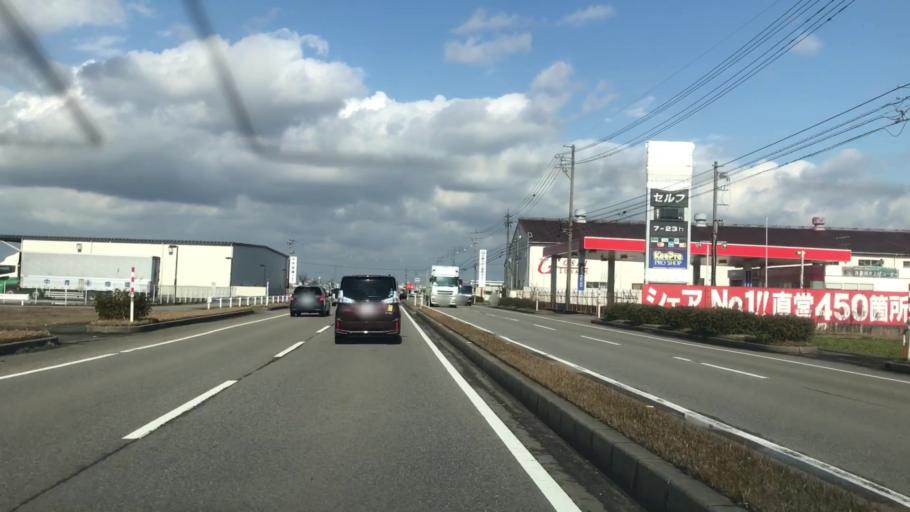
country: JP
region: Toyama
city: Kuragaki-kosugi
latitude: 36.7082
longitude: 137.0797
